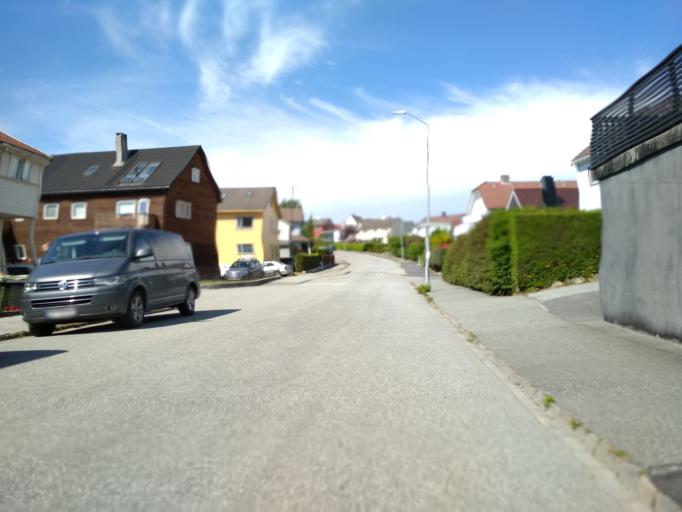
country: NO
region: Rogaland
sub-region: Stavanger
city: Stavanger
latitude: 58.9548
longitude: 5.7345
